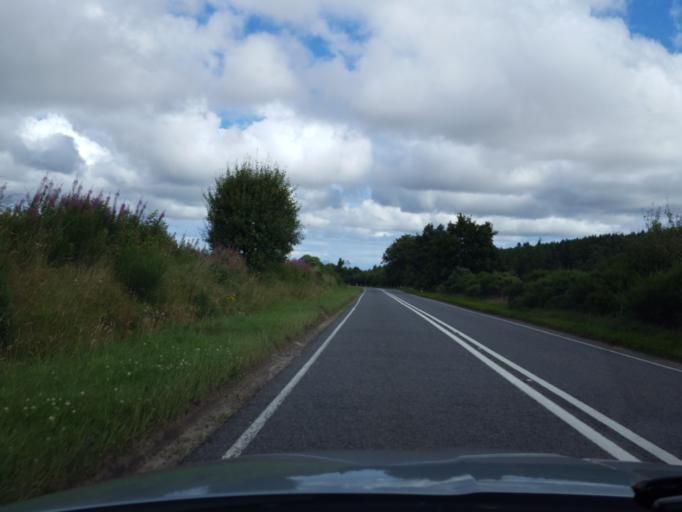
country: GB
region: Scotland
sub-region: Moray
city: Lhanbryd
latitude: 57.5870
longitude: -3.2796
